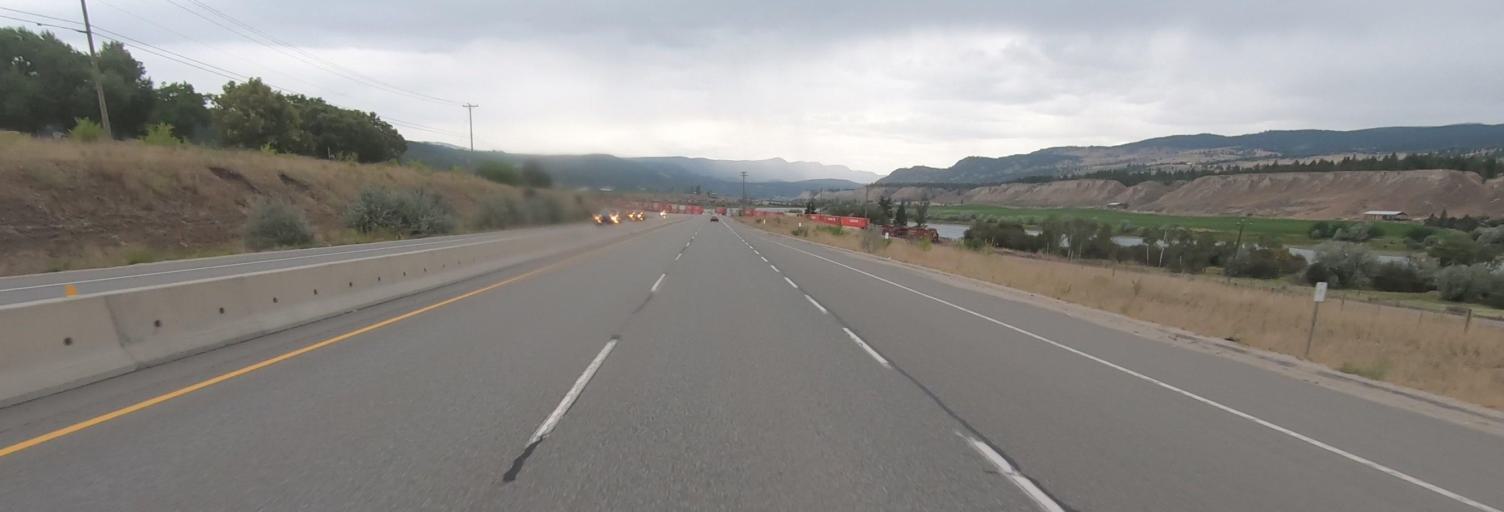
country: CA
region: British Columbia
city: Chase
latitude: 50.6822
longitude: -119.8173
